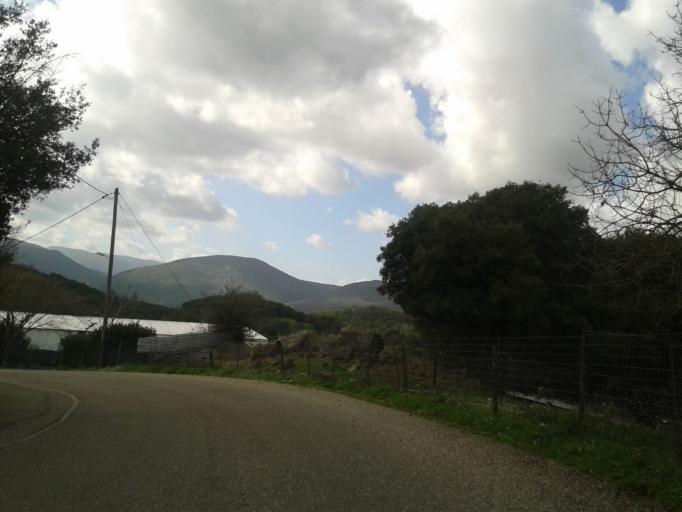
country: GR
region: West Greece
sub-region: Nomos Aitolias kai Akarnanias
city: Fitiai
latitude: 38.6399
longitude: 21.1771
